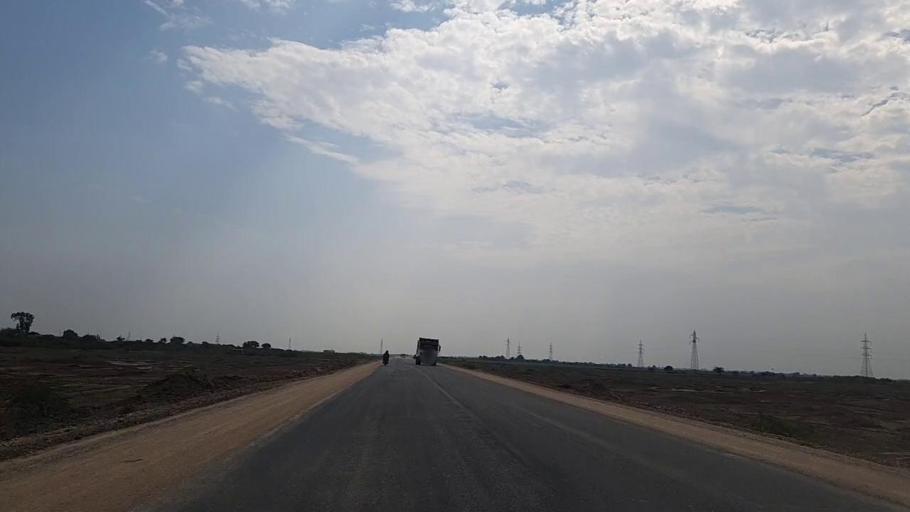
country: PK
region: Sindh
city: Naukot
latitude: 24.9617
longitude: 69.2828
